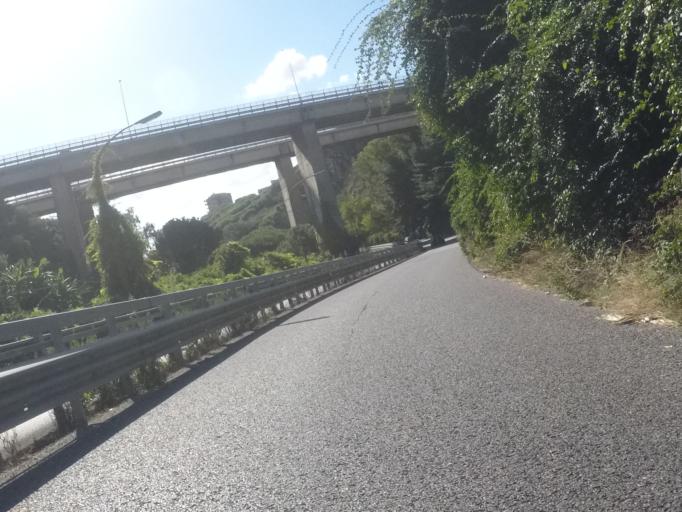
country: IT
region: Sicily
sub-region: Messina
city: Messina
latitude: 38.2010
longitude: 15.5420
